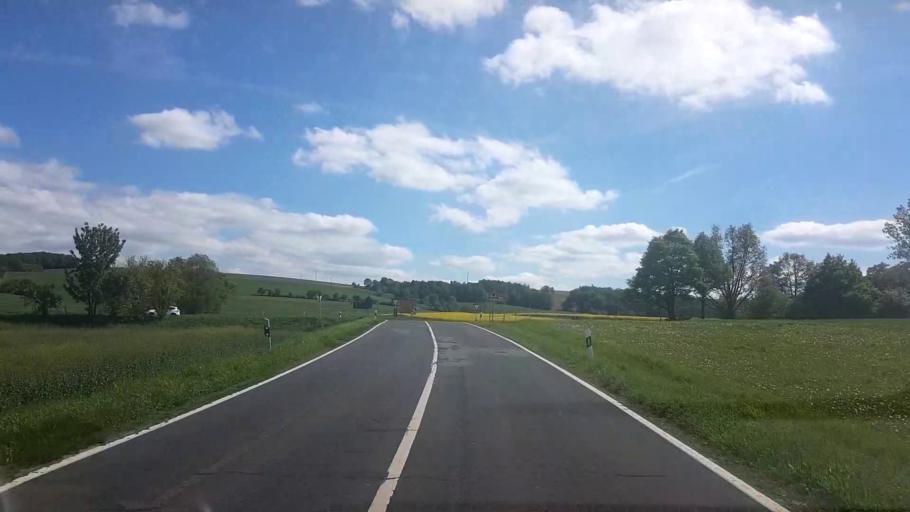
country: DE
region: Bavaria
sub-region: Regierungsbezirk Unterfranken
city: Untermerzbach
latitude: 50.1272
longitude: 10.8849
